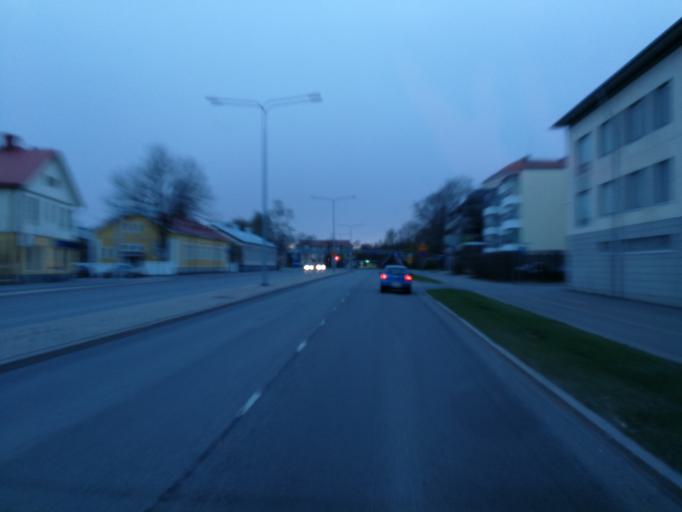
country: FI
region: Varsinais-Suomi
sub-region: Turku
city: Turku
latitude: 60.4611
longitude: 22.2651
